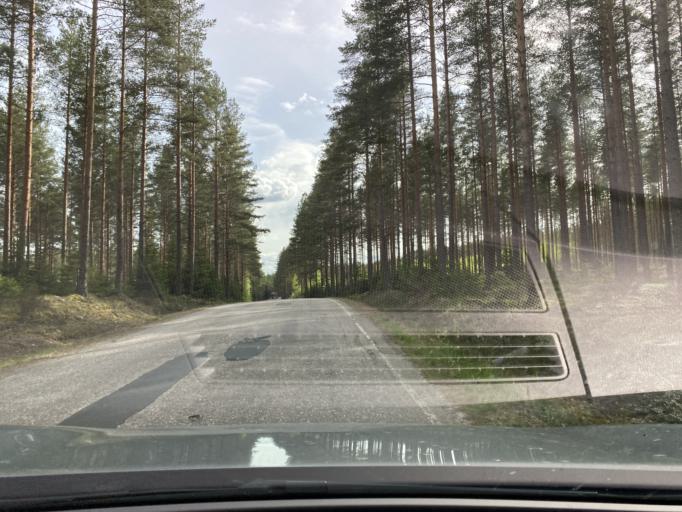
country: FI
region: Varsinais-Suomi
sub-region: Salo
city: Kiikala
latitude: 60.4847
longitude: 23.5434
